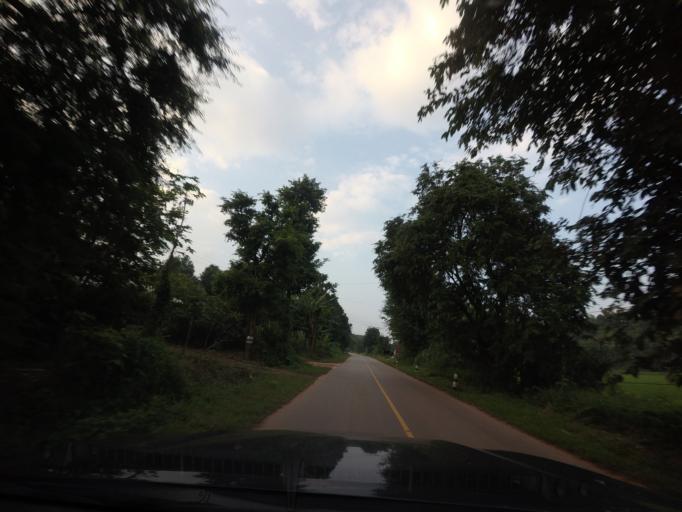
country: TH
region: Loei
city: Na Haeo
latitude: 17.3924
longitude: 101.0458
